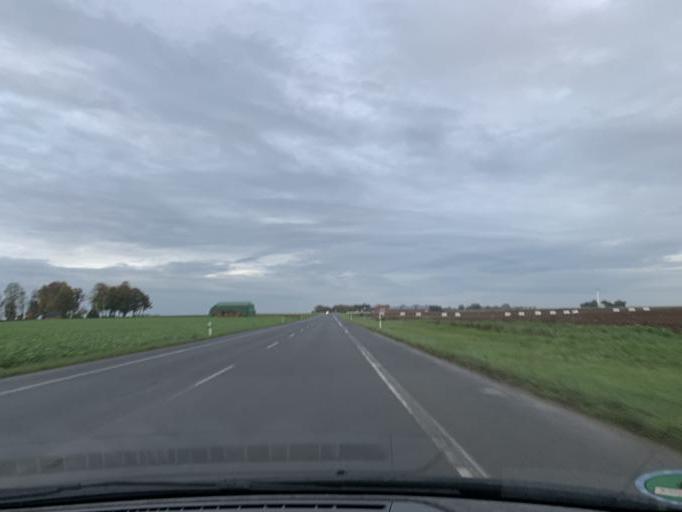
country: DE
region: North Rhine-Westphalia
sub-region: Regierungsbezirk Koln
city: Titz
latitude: 51.0101
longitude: 6.3909
